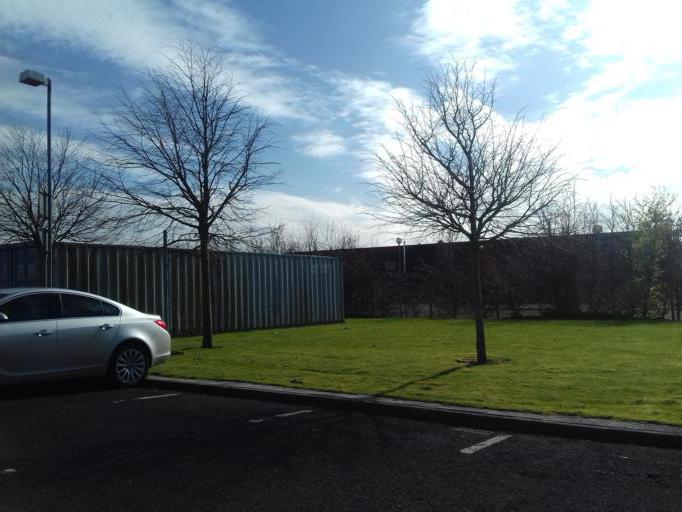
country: IE
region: Leinster
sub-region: Fingal County
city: Blanchardstown
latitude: 53.4077
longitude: -6.3607
